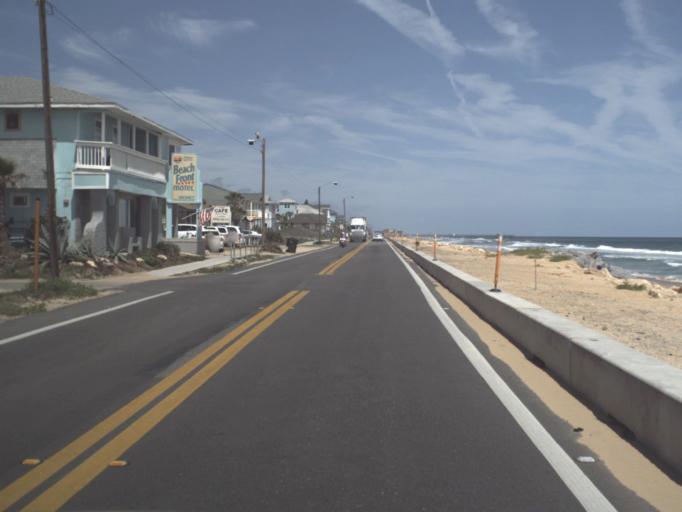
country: US
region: Florida
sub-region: Flagler County
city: Flagler Beach
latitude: 29.4671
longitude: -81.1207
